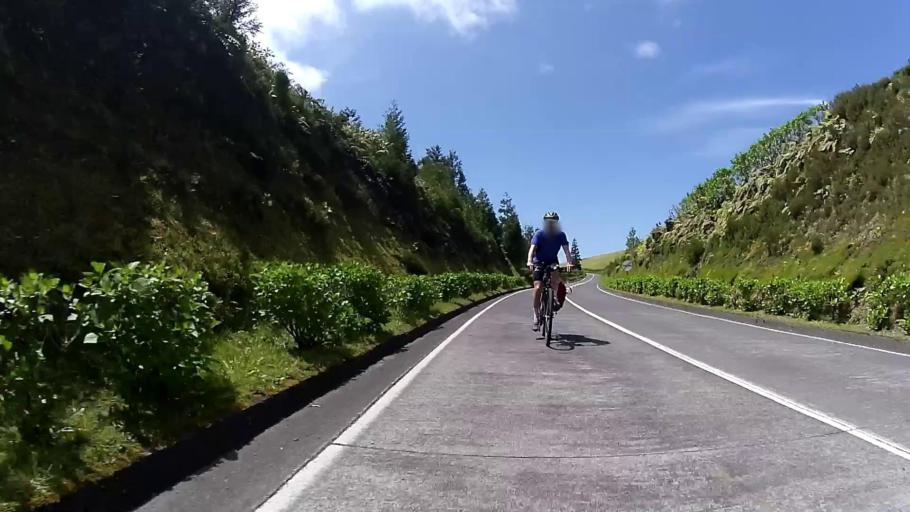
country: PT
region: Azores
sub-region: Ponta Delgada
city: Arrifes
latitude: 37.8446
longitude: -25.7698
